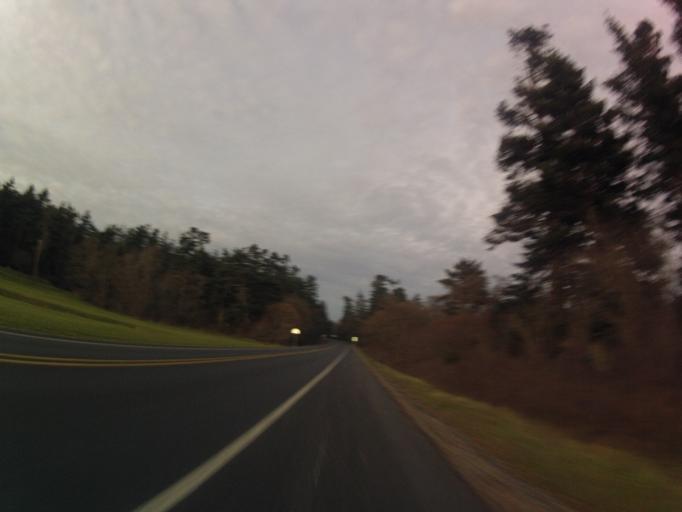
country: US
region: Washington
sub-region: Island County
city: Coupeville
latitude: 48.1664
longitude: -122.6794
